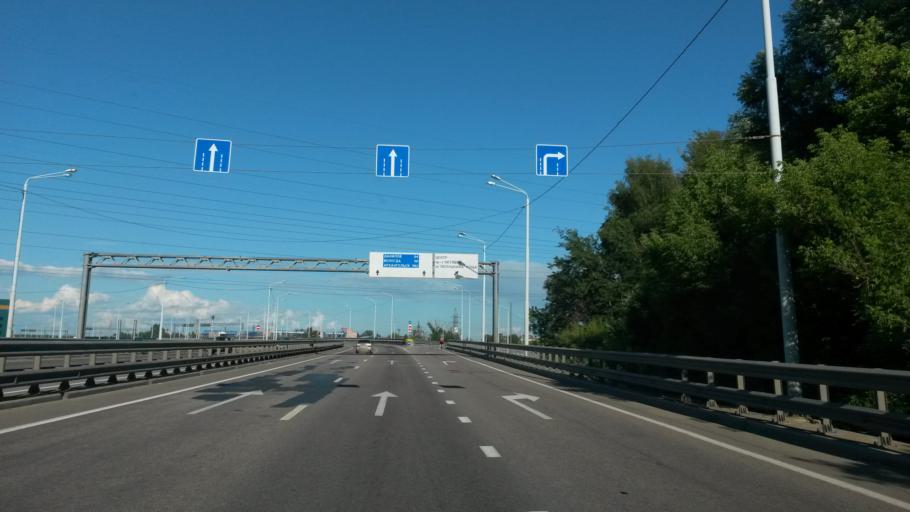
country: RU
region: Jaroslavl
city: Yaroslavl
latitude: 57.6684
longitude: 39.8344
